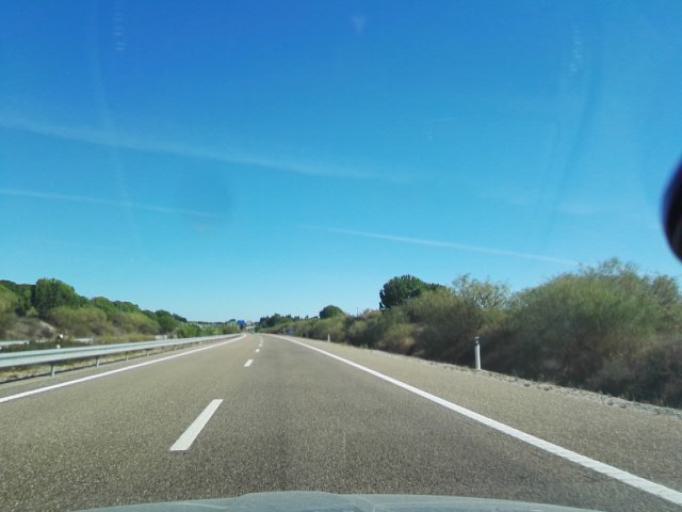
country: PT
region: Evora
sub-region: Vendas Novas
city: Vendas Novas
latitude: 38.6776
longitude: -8.6418
